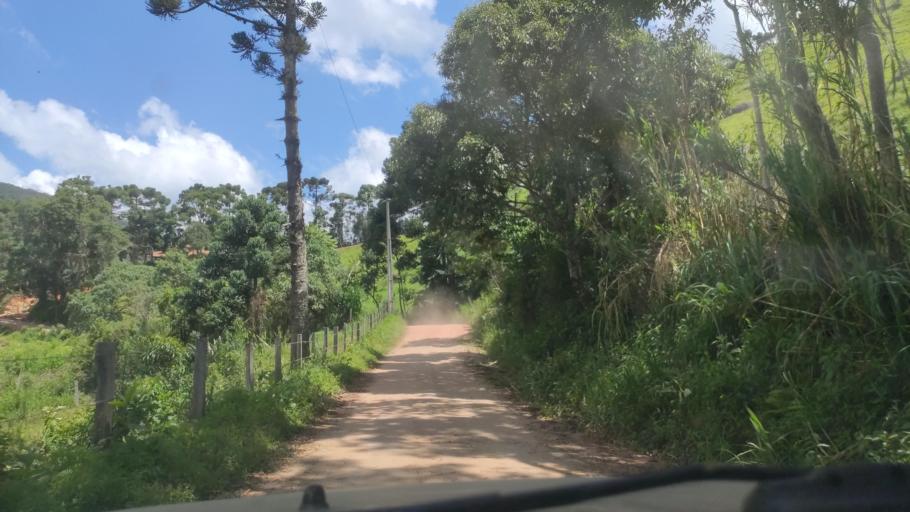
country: BR
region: Minas Gerais
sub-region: Cambui
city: Cambui
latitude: -22.6830
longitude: -45.9771
